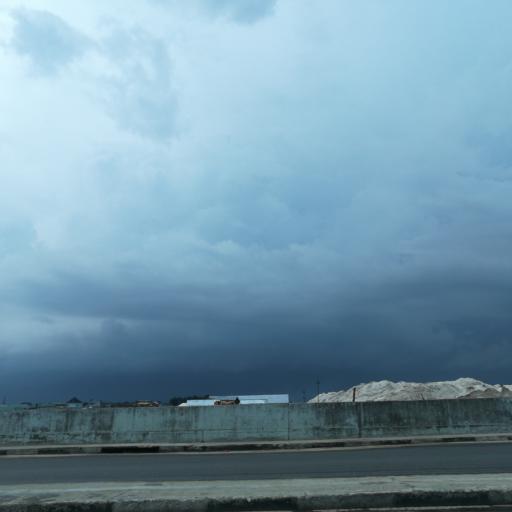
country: NG
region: Rivers
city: Port Harcourt
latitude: 4.8046
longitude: 7.0588
